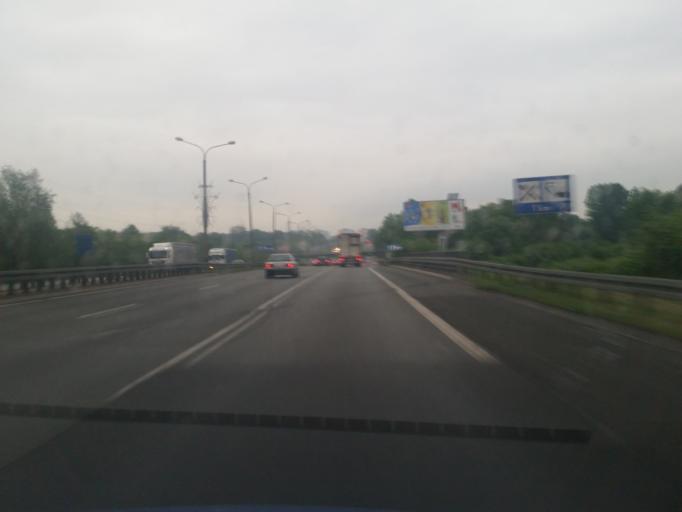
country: PL
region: Silesian Voivodeship
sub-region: Sosnowiec
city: Sosnowiec
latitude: 50.2818
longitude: 19.0909
